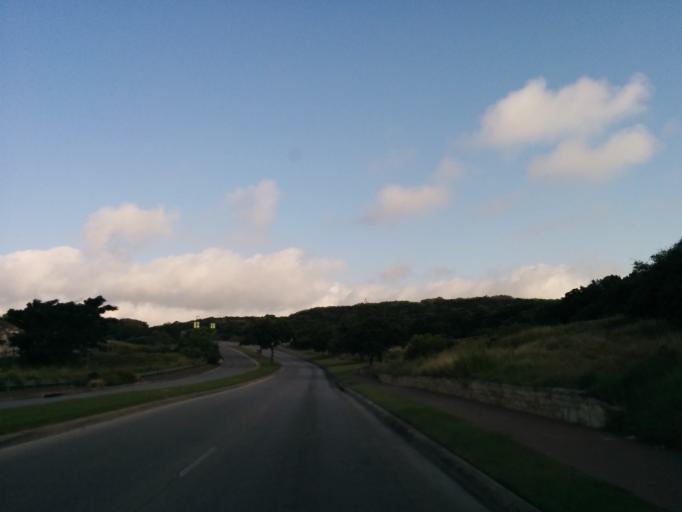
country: US
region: Texas
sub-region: Bexar County
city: Shavano Park
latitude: 29.6047
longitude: -98.6075
